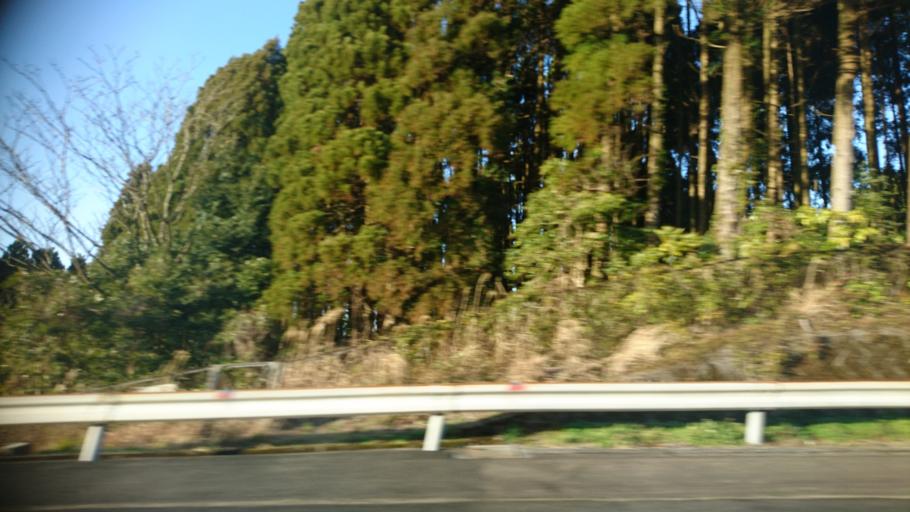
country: JP
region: Miyazaki
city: Miyazaki-shi
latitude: 31.8182
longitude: 131.2670
